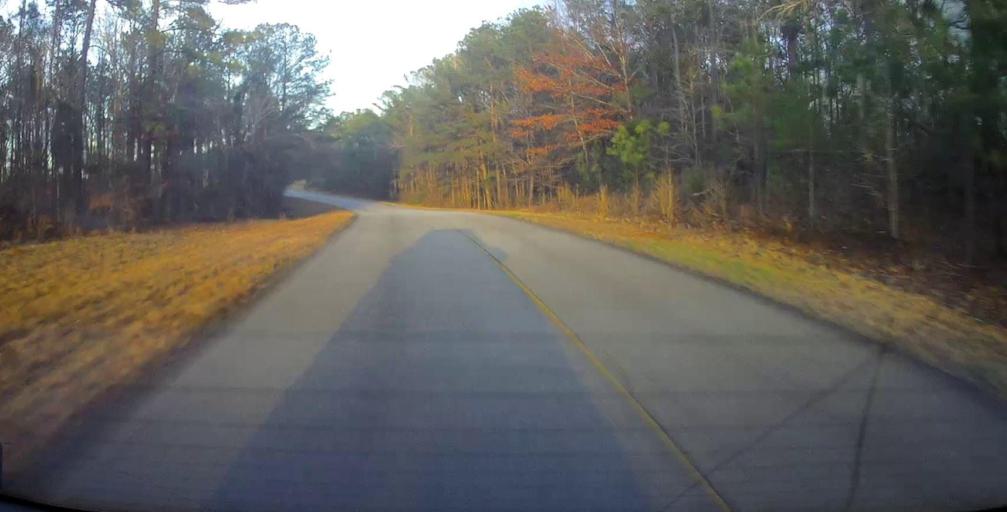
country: US
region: Georgia
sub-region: Harris County
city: Hamilton
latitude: 32.6051
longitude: -84.8731
